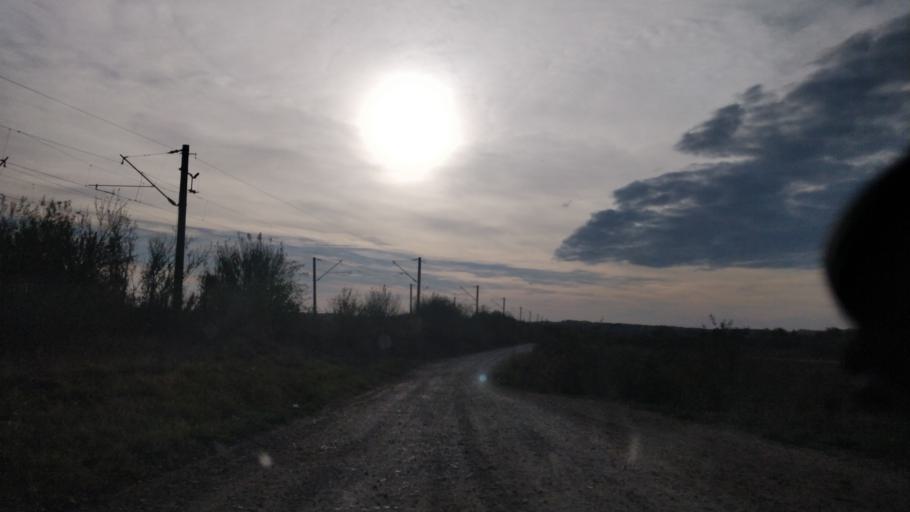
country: RO
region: Giurgiu
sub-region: Comuna Clejani
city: Clejani
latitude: 44.3404
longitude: 25.6936
